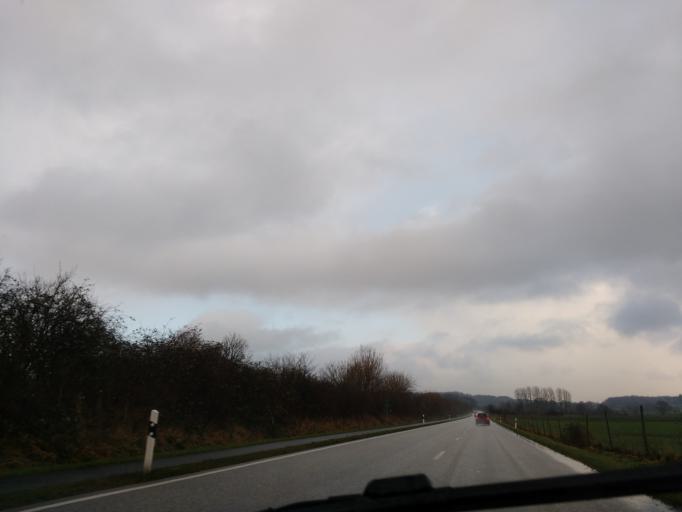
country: DE
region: Schleswig-Holstein
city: Gross Wittensee
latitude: 54.4120
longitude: 9.7743
